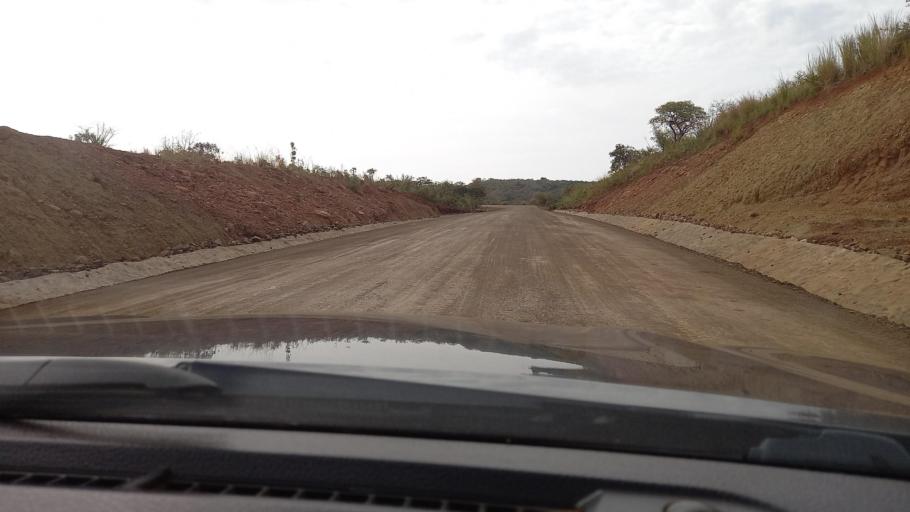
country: ET
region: Southern Nations, Nationalities, and People's Region
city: Mizan Teferi
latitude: 6.1912
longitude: 35.6860
